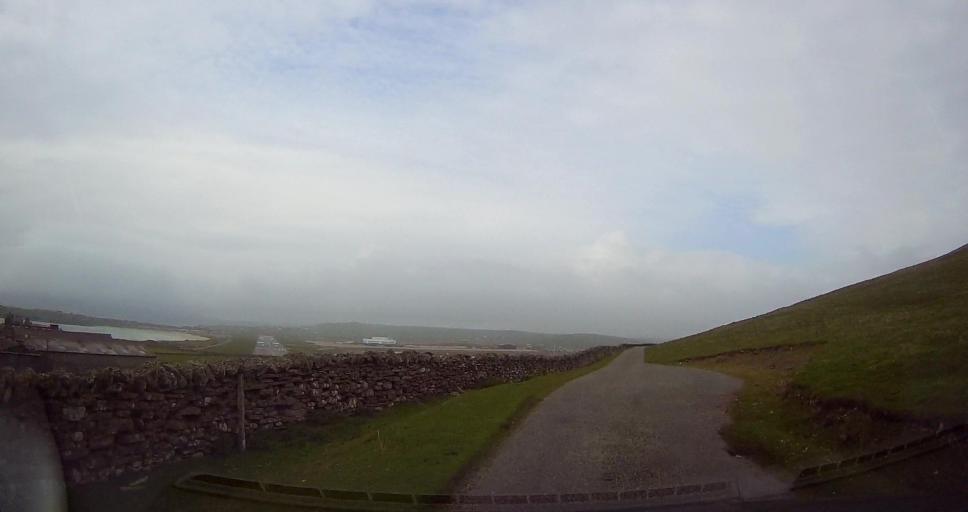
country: GB
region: Scotland
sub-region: Shetland Islands
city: Sandwick
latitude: 59.8670
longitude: -1.2789
